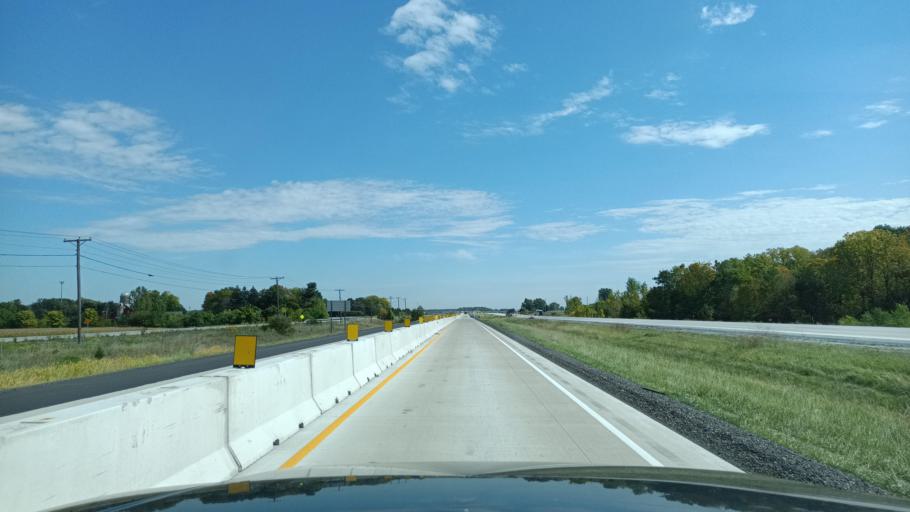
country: US
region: Indiana
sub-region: Allen County
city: New Haven
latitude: 41.1081
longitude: -84.9515
